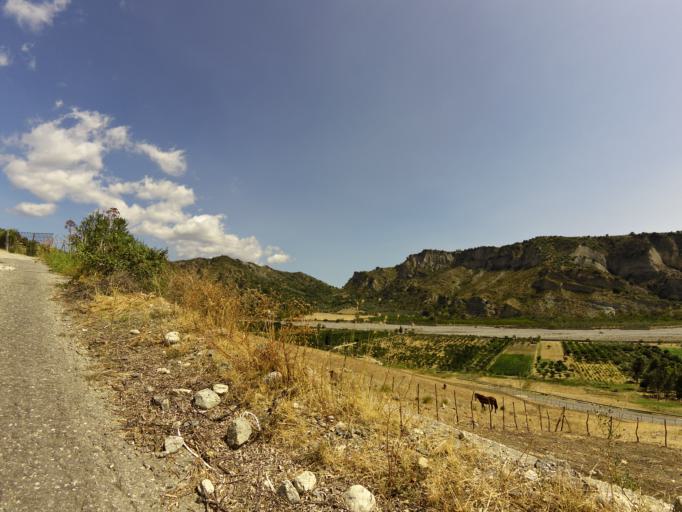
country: IT
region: Calabria
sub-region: Provincia di Reggio Calabria
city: Stilo
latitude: 38.4749
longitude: 16.4781
